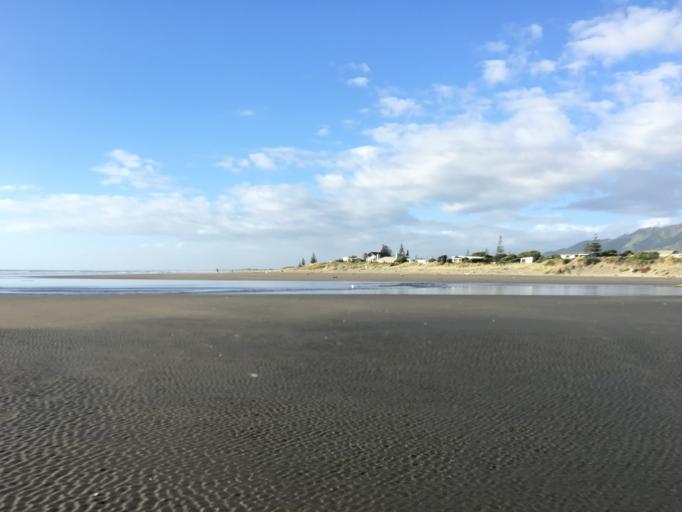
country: NZ
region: Wellington
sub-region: Kapiti Coast District
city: Paraparaumu
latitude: -40.8575
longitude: 175.0278
